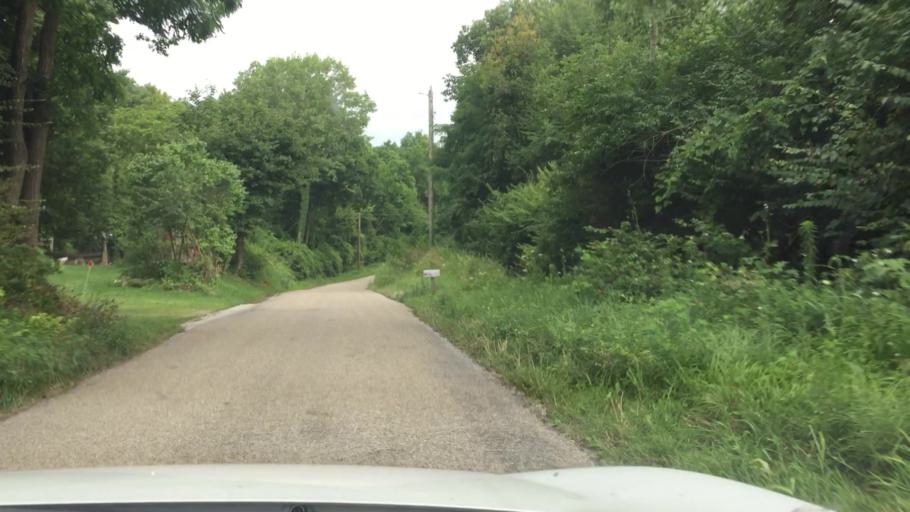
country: US
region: Ohio
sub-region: Champaign County
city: Mechanicsburg
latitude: 40.0536
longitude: -83.6402
